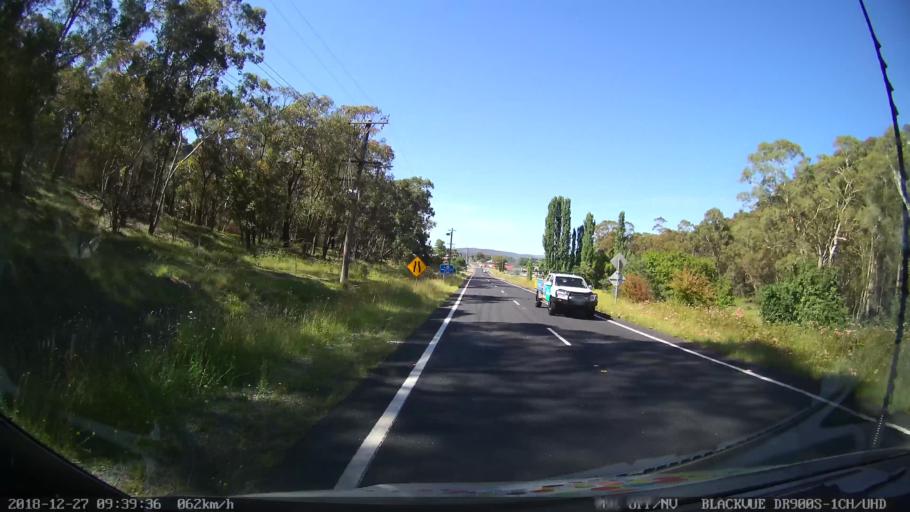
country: AU
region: New South Wales
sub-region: Lithgow
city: Portland
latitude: -33.2945
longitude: 150.0346
